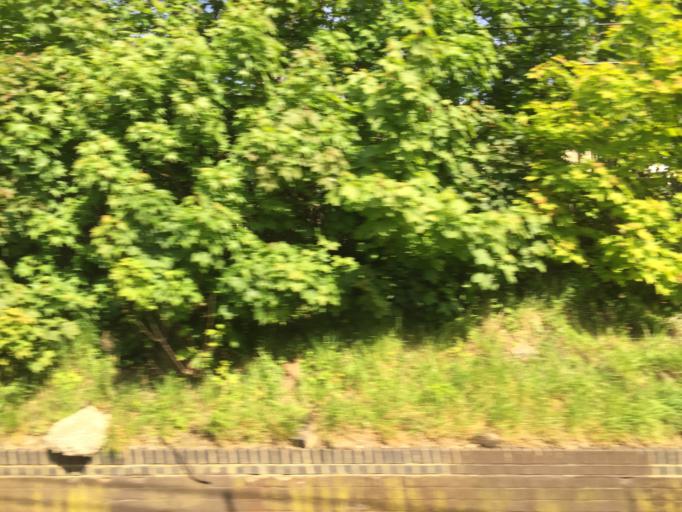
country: GB
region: England
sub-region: Greater London
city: Ilford
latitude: 51.5635
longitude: 0.0923
